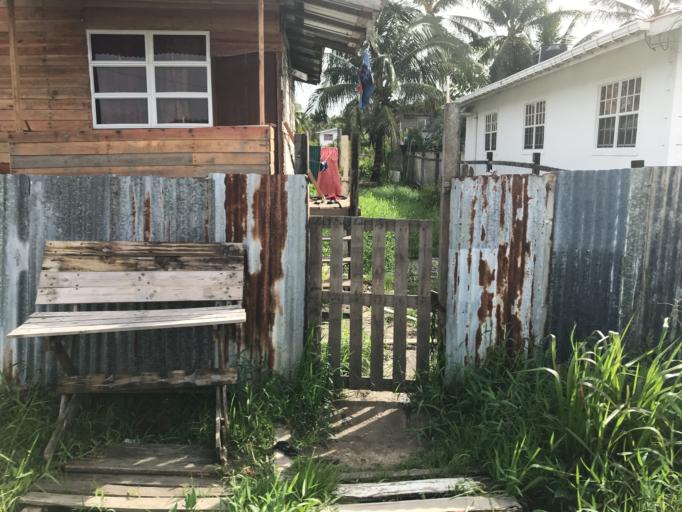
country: GY
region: Demerara-Mahaica
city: Georgetown
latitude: 6.7932
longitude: -58.1282
